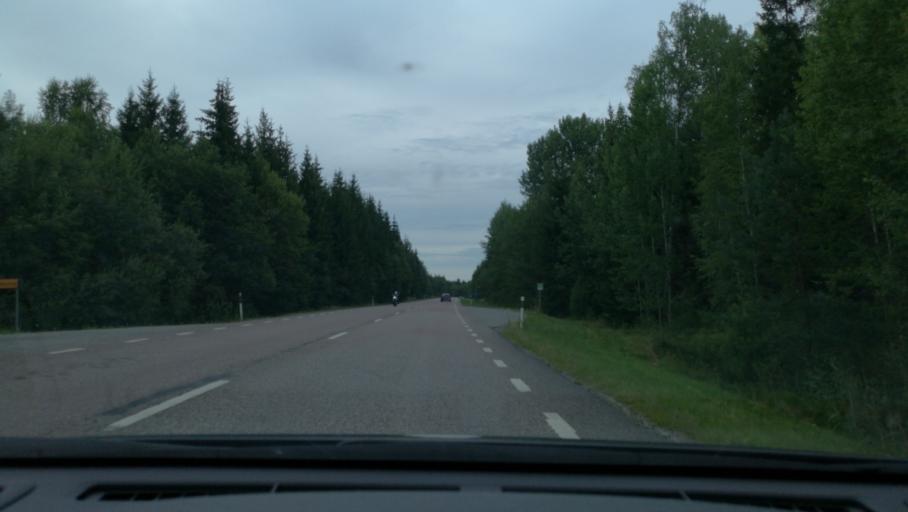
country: SE
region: Soedermanland
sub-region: Katrineholms Kommun
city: Katrineholm
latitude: 59.0265
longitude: 16.2137
